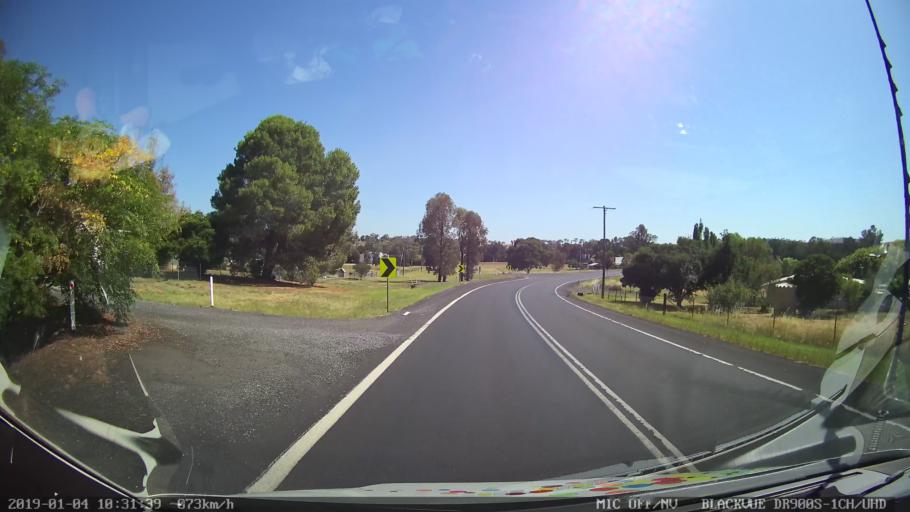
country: AU
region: New South Wales
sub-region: Cabonne
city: Canowindra
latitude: -33.3323
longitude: 148.6327
